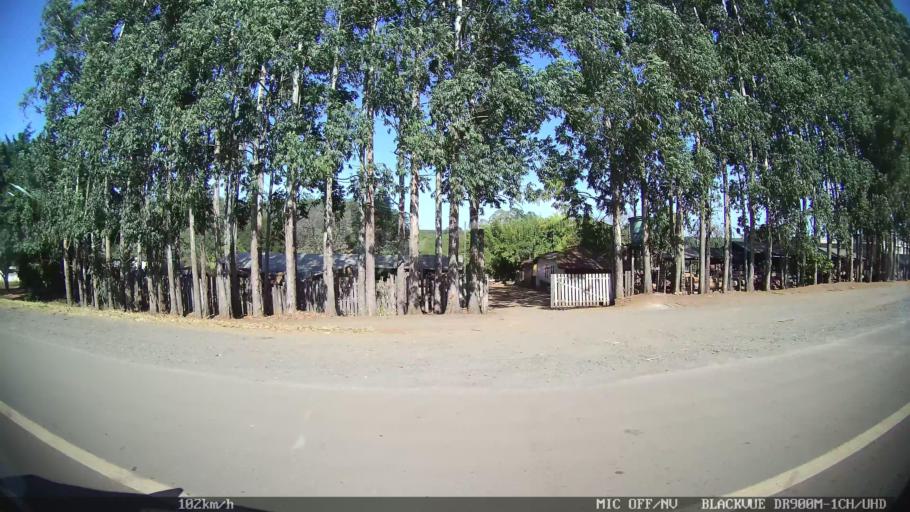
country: BR
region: Sao Paulo
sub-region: Batatais
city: Batatais
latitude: -20.9071
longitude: -47.5966
